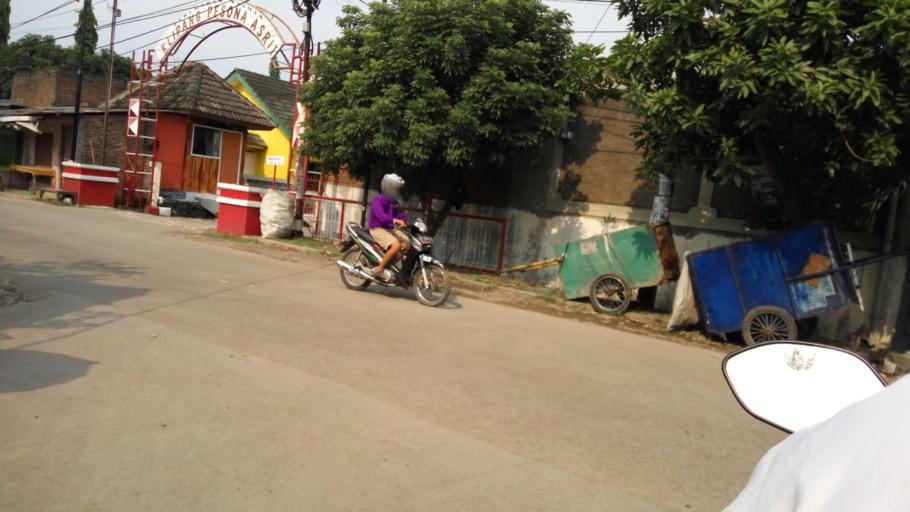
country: ID
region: Central Java
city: Mranggen
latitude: -7.0380
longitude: 110.4751
